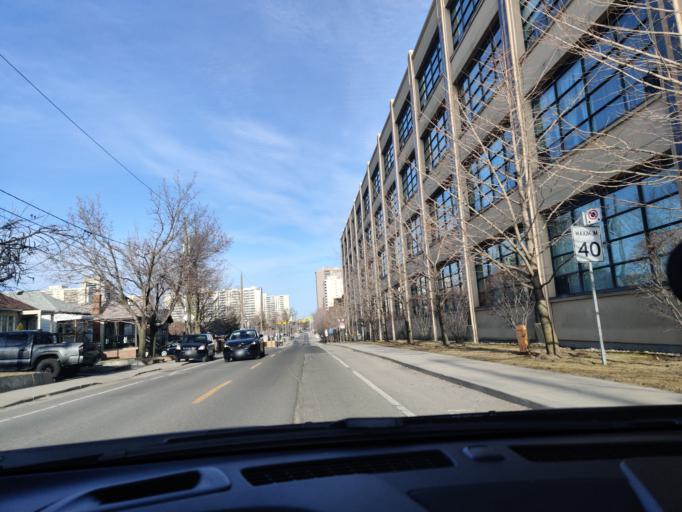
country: CA
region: Ontario
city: Toronto
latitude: 43.7006
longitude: -79.4476
